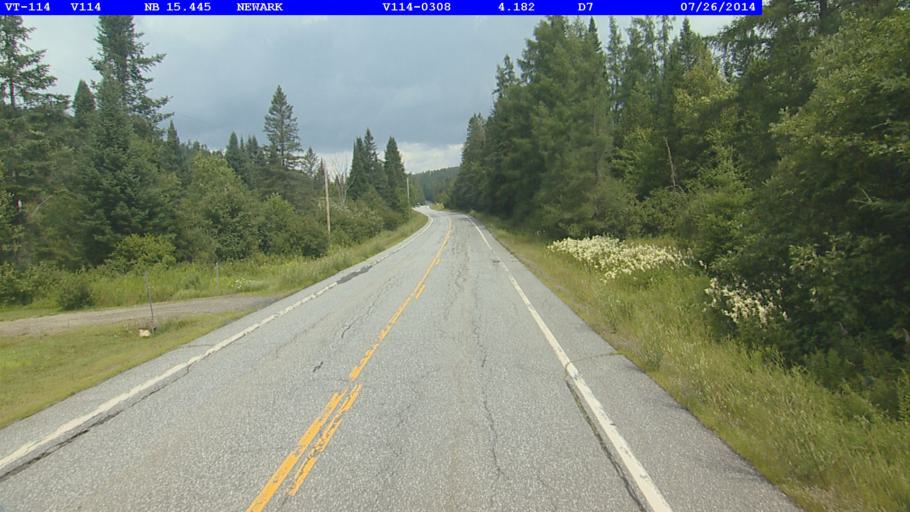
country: US
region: Vermont
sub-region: Caledonia County
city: Lyndonville
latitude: 44.7263
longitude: -71.8744
